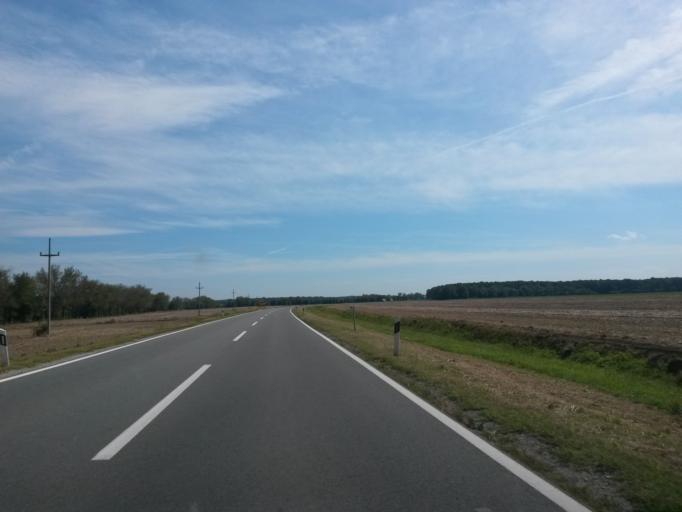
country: HR
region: Vukovarsko-Srijemska
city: Vinkovci
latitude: 45.2556
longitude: 18.8141
